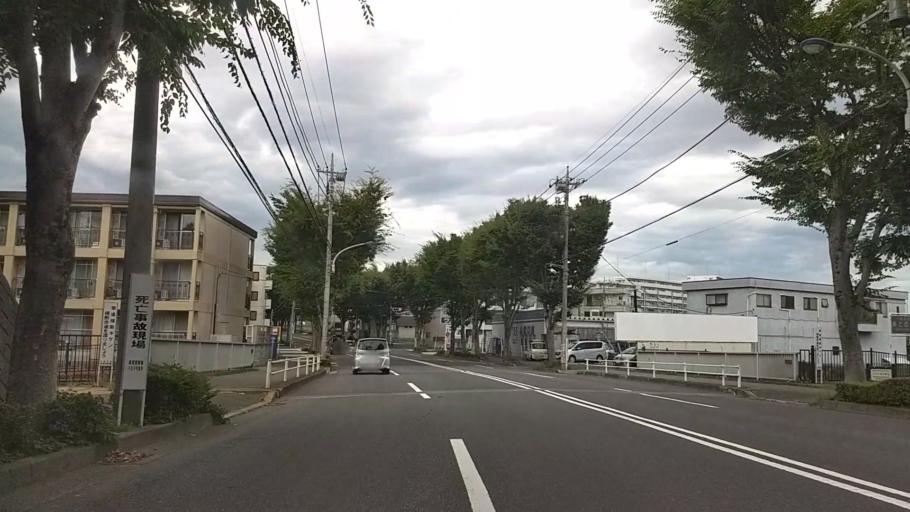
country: JP
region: Tokyo
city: Hachioji
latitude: 35.6319
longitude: 139.3120
